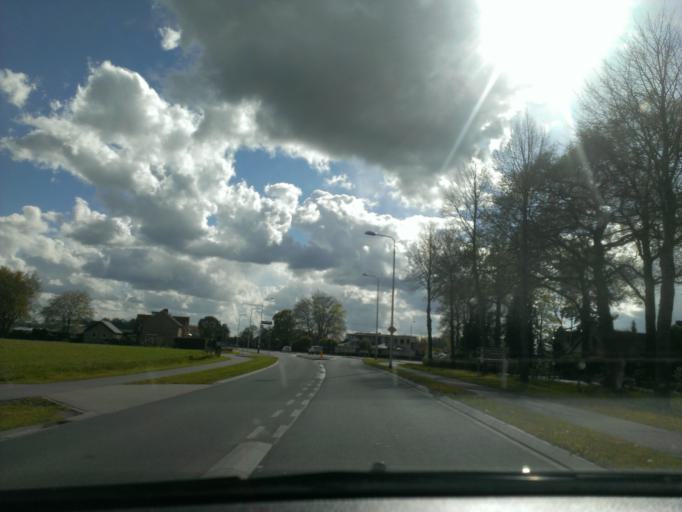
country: NL
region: Gelderland
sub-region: Gemeente Voorst
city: Twello
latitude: 52.2360
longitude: 6.0493
